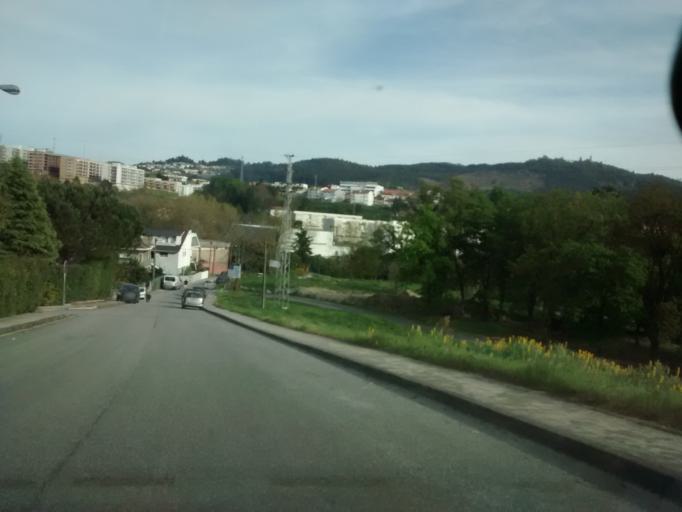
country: PT
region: Braga
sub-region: Guimaraes
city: Guimaraes
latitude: 41.4554
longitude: -8.2900
